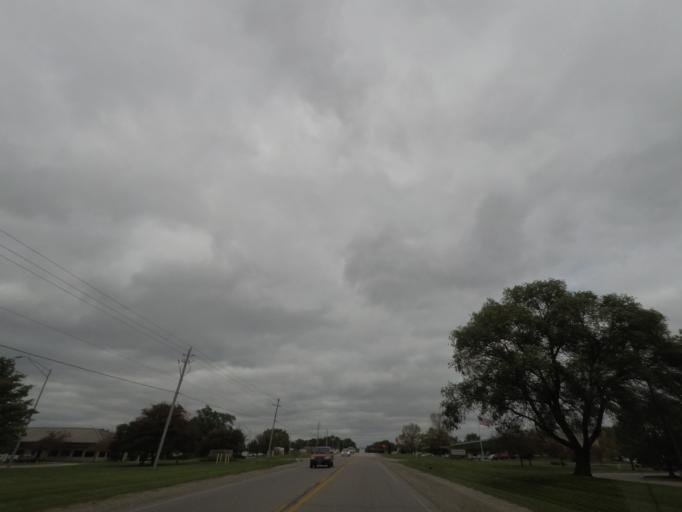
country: US
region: Iowa
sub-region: Polk County
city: Saylorville
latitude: 41.6857
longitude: -93.6002
